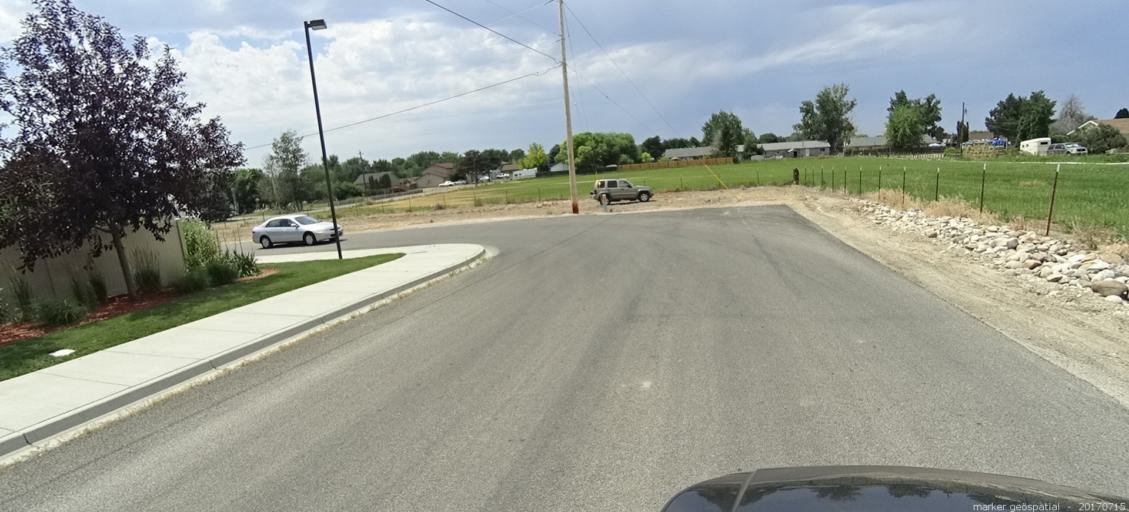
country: US
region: Idaho
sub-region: Ada County
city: Garden City
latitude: 43.5694
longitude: -116.3073
